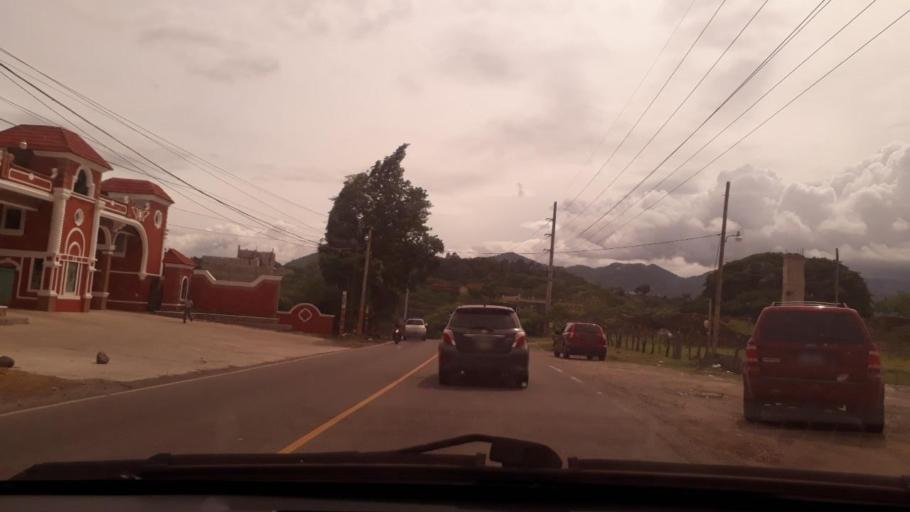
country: GT
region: Jutiapa
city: El Progreso
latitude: 14.3479
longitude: -89.8413
